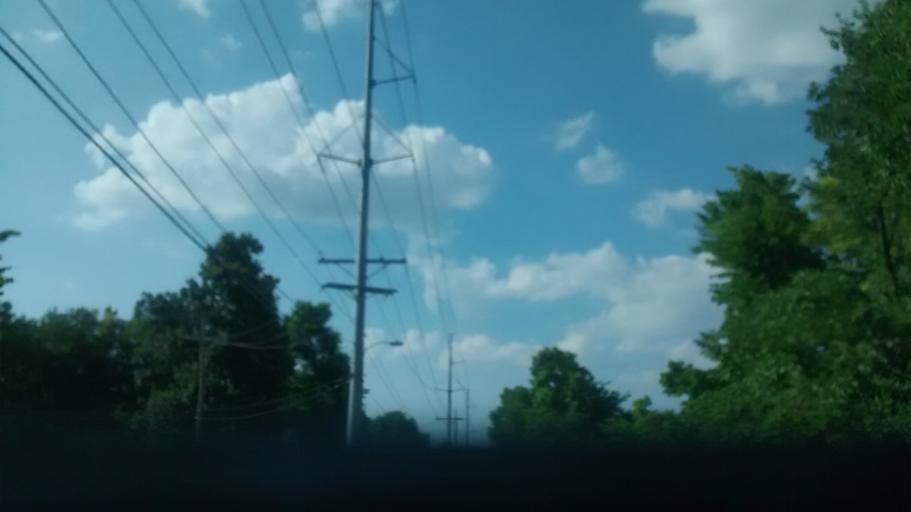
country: US
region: Arkansas
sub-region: Washington County
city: Fayetteville
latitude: 36.0713
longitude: -94.1676
